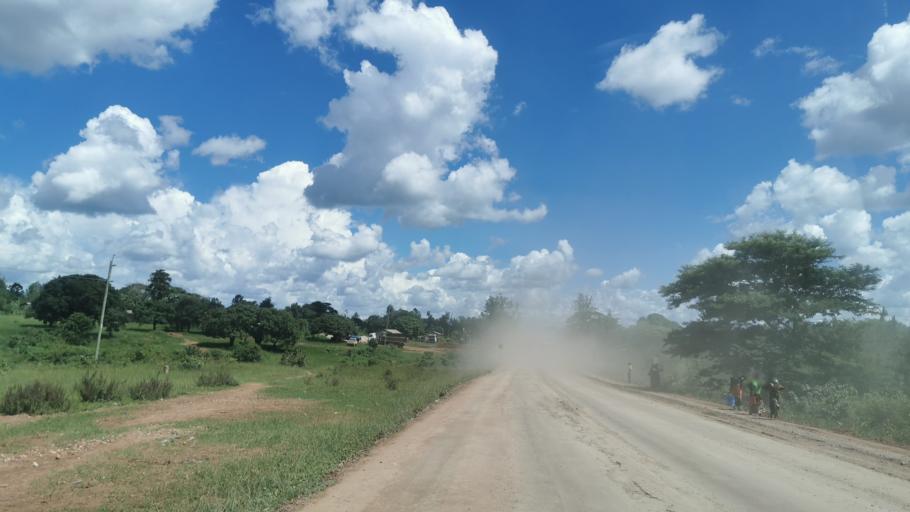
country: TZ
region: Kagera
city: Biharamulo
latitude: -2.9057
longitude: 31.1927
